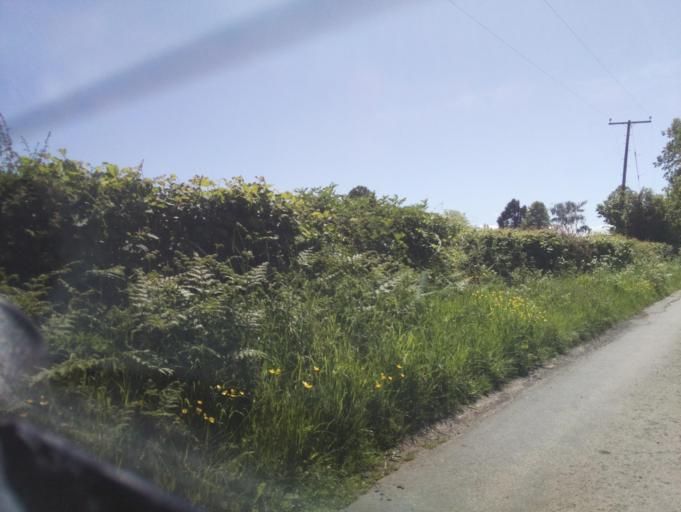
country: GB
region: Wales
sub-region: Monmouthshire
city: Magor
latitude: 51.5912
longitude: -2.8208
